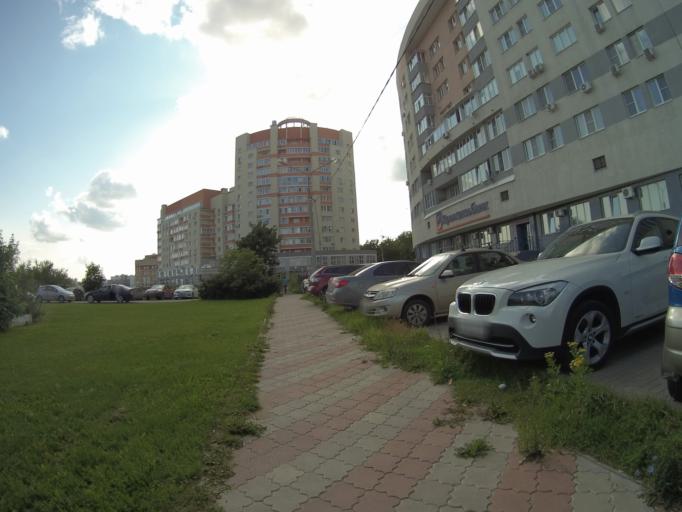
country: RU
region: Vladimir
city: Vladimir
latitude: 56.1389
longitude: 40.3884
